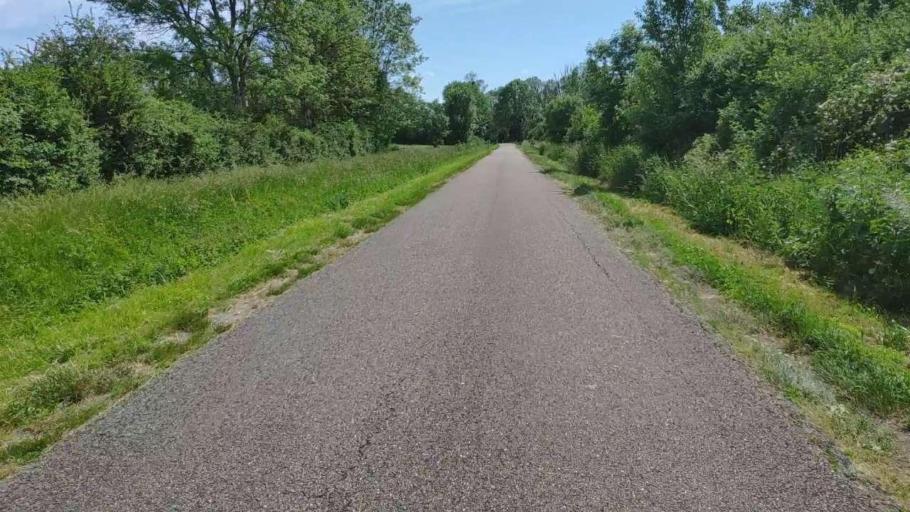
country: FR
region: Franche-Comte
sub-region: Departement du Jura
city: Bletterans
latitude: 46.7244
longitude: 5.4770
